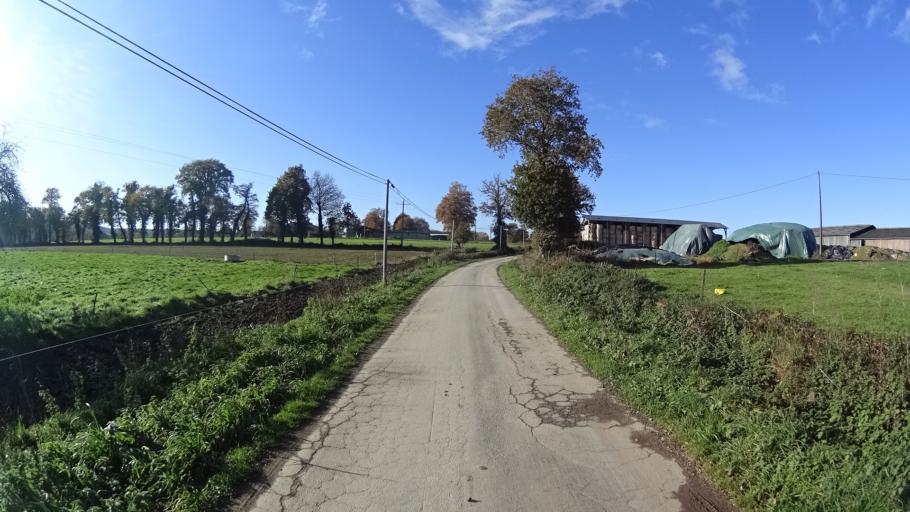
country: FR
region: Brittany
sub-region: Departement du Morbihan
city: Carentoir
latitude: 47.7910
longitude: -2.1693
